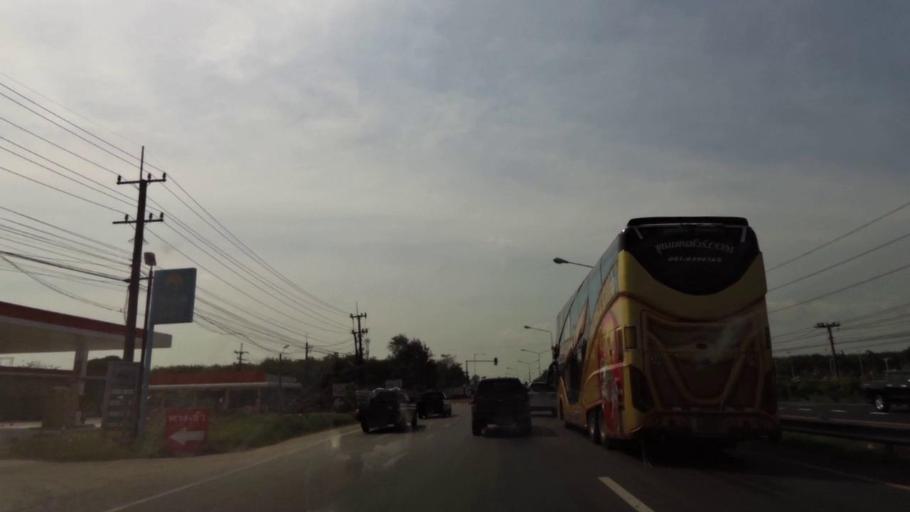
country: TH
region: Chanthaburi
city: Chanthaburi
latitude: 12.6620
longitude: 102.0739
